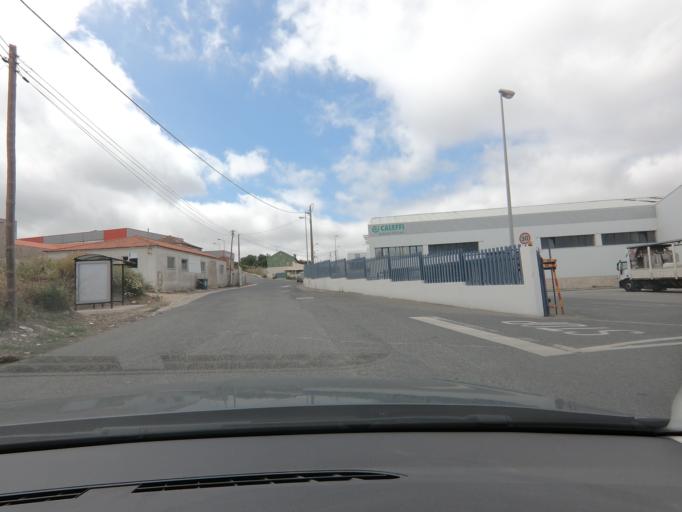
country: PT
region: Lisbon
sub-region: Oeiras
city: Porto Salvo
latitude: 38.7423
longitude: -9.3158
